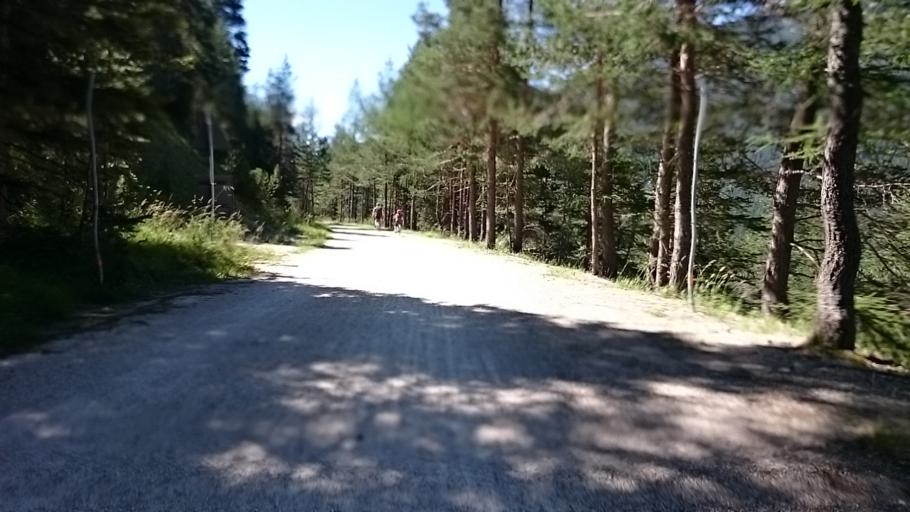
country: IT
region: Veneto
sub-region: Provincia di Belluno
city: Cortina d'Ampezzo
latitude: 46.5911
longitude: 12.1155
